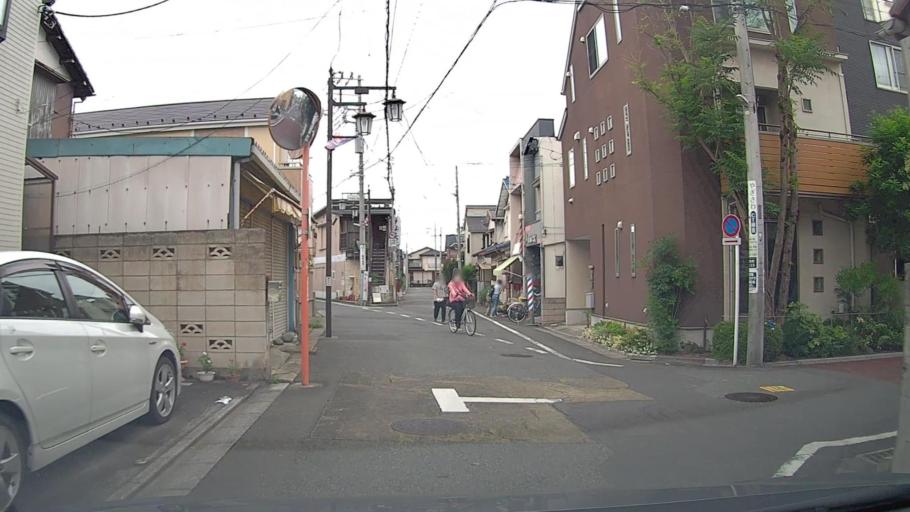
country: JP
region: Tokyo
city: Nishi-Tokyo-shi
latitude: 35.7297
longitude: 139.5506
